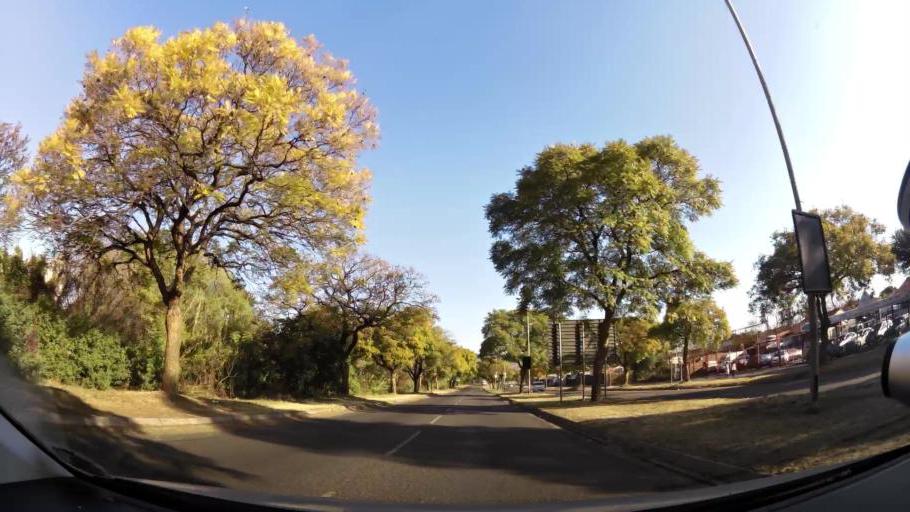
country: ZA
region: Gauteng
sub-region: City of Tshwane Metropolitan Municipality
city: Pretoria
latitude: -25.7556
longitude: 28.1428
